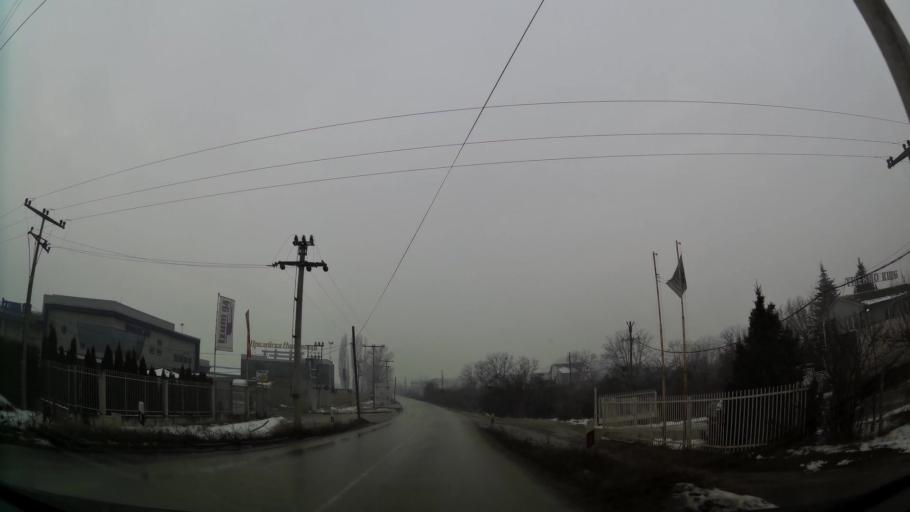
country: MK
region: Ilinden
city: Idrizovo
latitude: 41.9580
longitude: 21.5830
